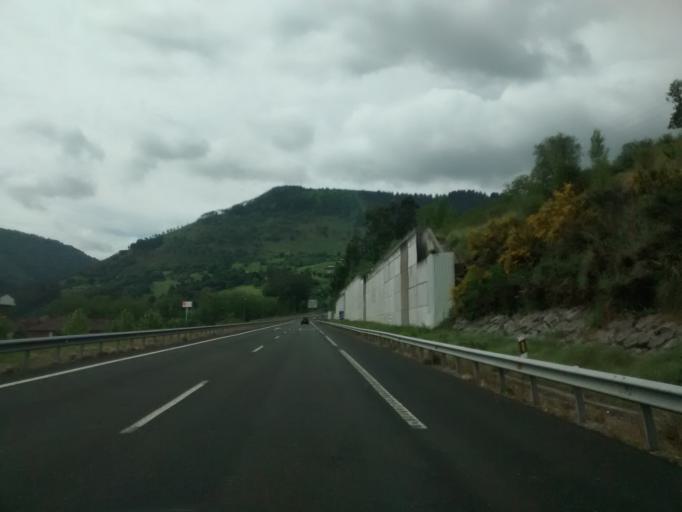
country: ES
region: Cantabria
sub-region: Provincia de Cantabria
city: Los Corrales de Buelna
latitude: 43.2577
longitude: -4.0722
